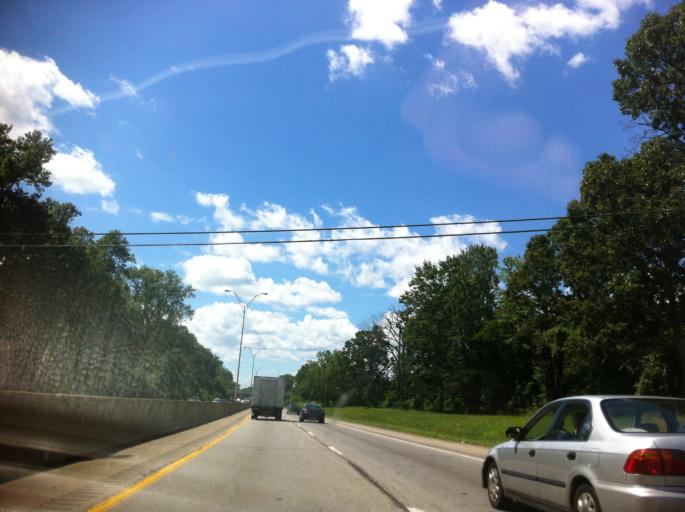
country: US
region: Ohio
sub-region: Lucas County
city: Ottawa Hills
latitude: 41.6884
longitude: -83.6300
